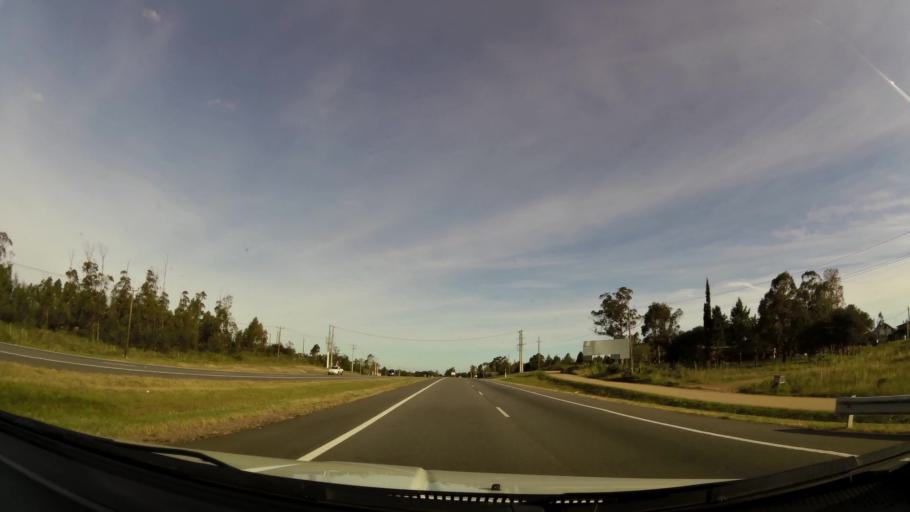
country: UY
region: Canelones
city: La Floresta
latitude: -34.7732
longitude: -55.5713
